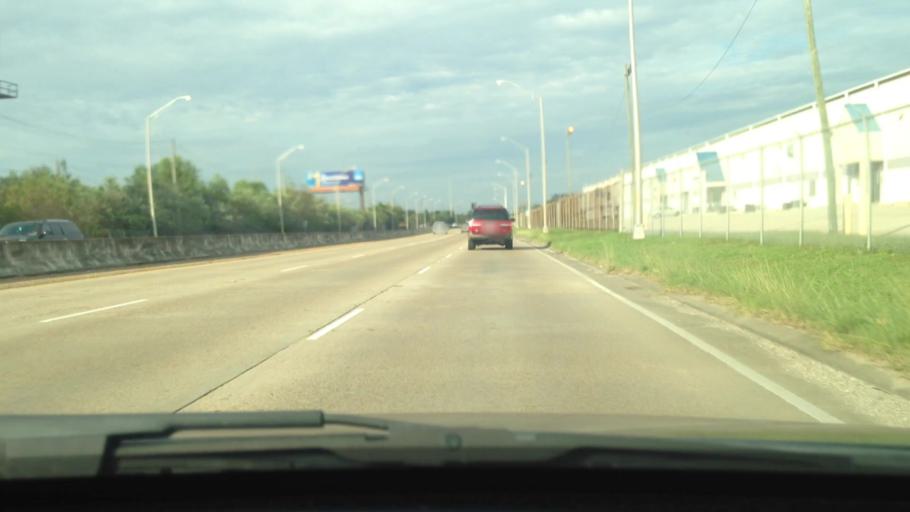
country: US
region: Louisiana
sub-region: Jefferson Parish
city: Jefferson
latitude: 29.9701
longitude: -90.1466
